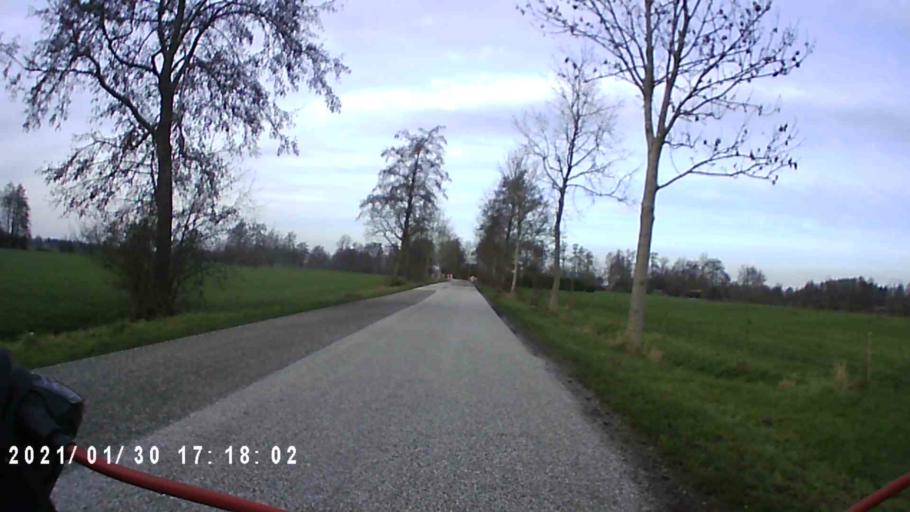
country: NL
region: Groningen
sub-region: Gemeente Leek
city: Leek
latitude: 53.1842
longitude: 6.3579
